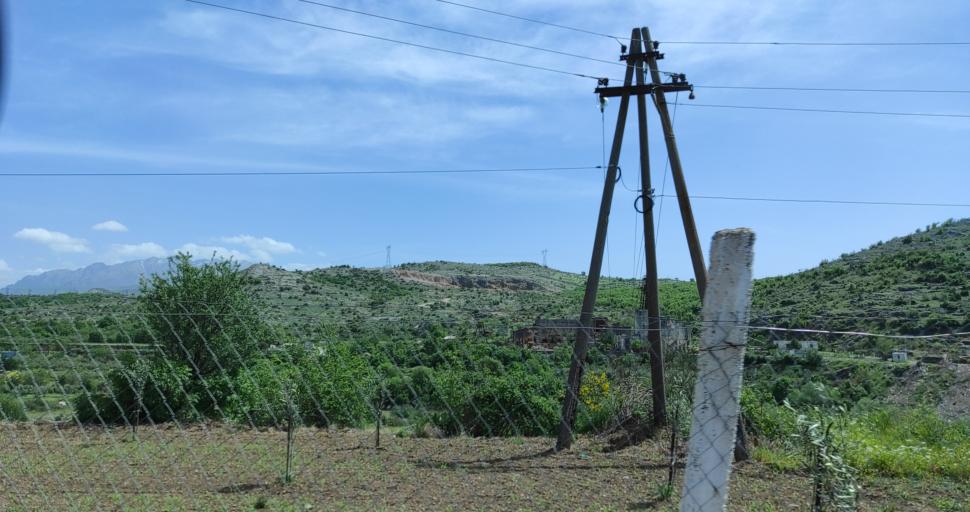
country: AL
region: Shkoder
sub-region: Rrethi i Malesia e Madhe
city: Gruemire
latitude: 42.1175
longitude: 19.5758
